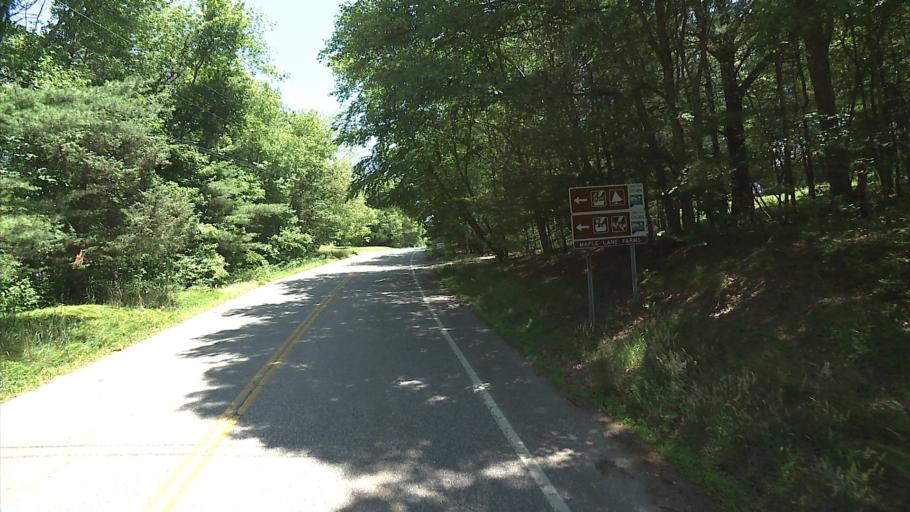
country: US
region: Connecticut
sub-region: New London County
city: Preston City
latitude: 41.4951
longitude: -71.9014
